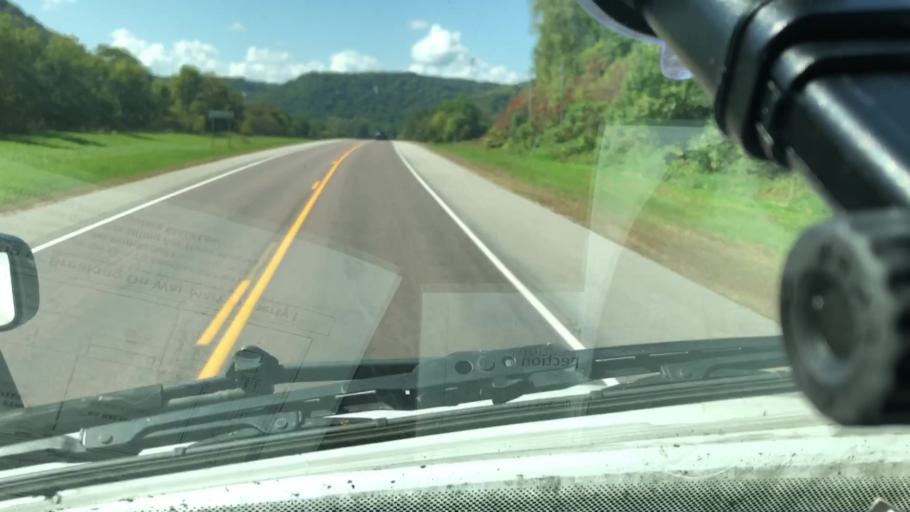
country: US
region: Minnesota
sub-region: Winona County
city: Winona
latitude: 44.0225
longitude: -91.6416
